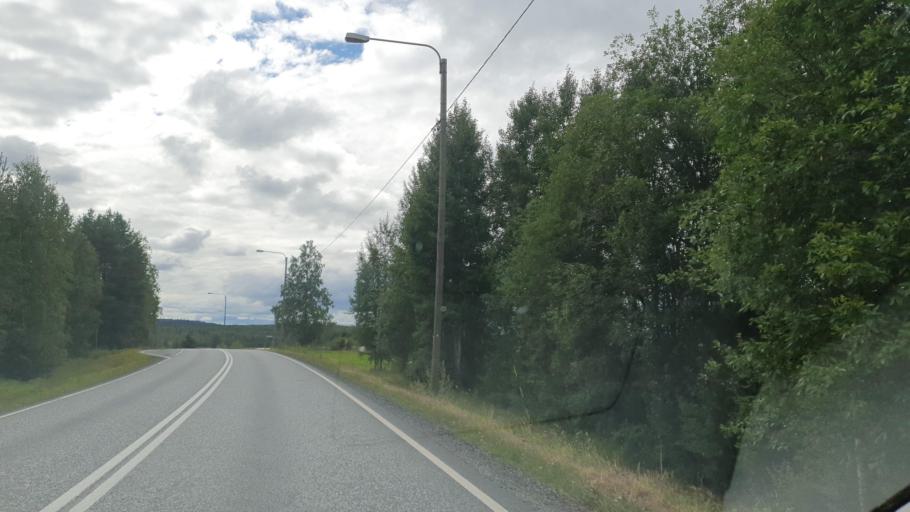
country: FI
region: Northern Savo
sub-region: Ylae-Savo
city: Iisalmi
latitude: 63.5212
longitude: 27.1409
